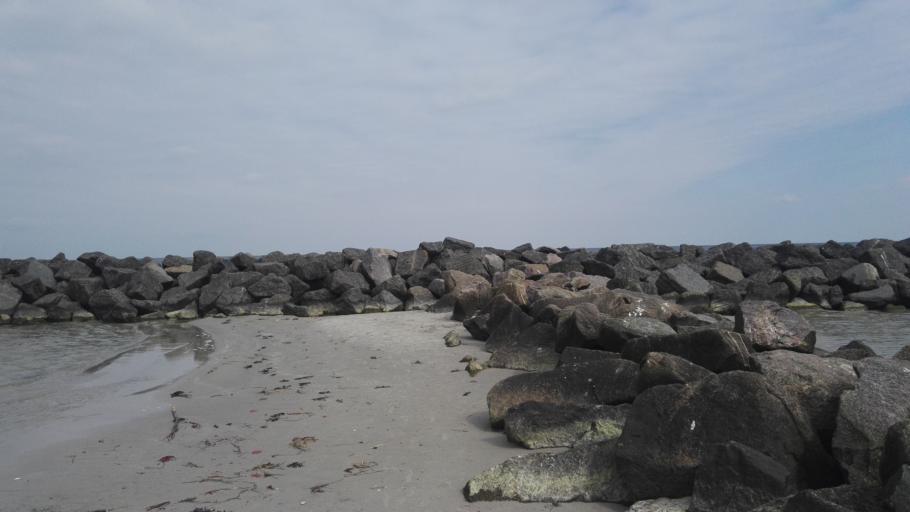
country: DE
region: Schleswig-Holstein
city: Stakendorf
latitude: 54.4116
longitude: 10.4229
